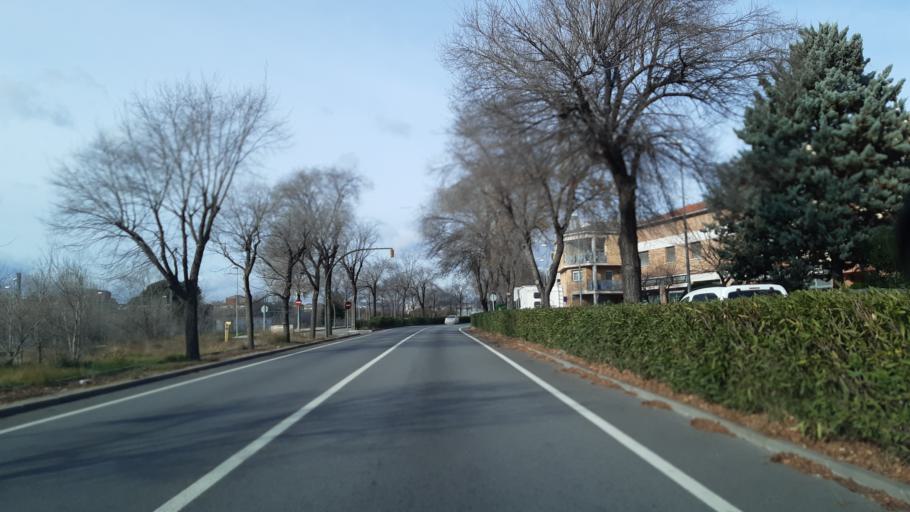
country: ES
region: Catalonia
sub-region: Provincia de Barcelona
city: Vilanova del Cami
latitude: 41.5723
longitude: 1.6451
